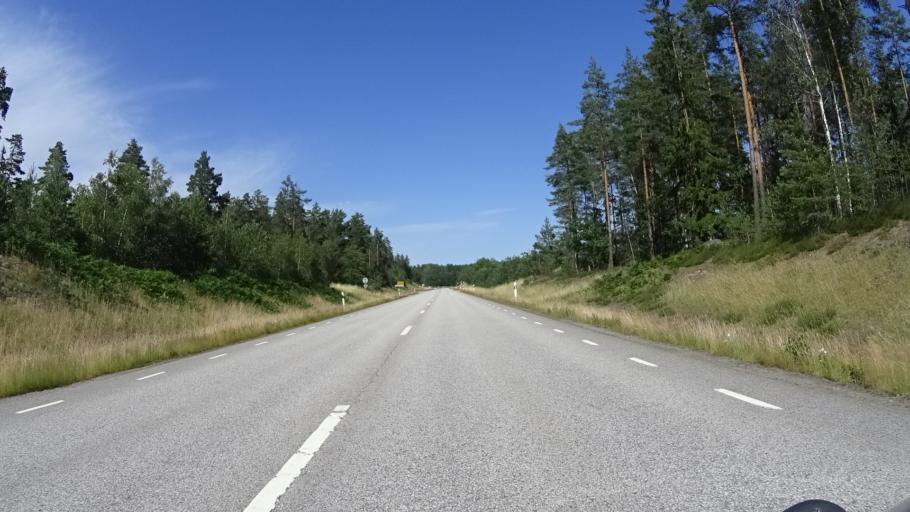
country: SE
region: Kalmar
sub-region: Vasterviks Kommun
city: Gamleby
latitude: 57.9331
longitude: 16.3801
